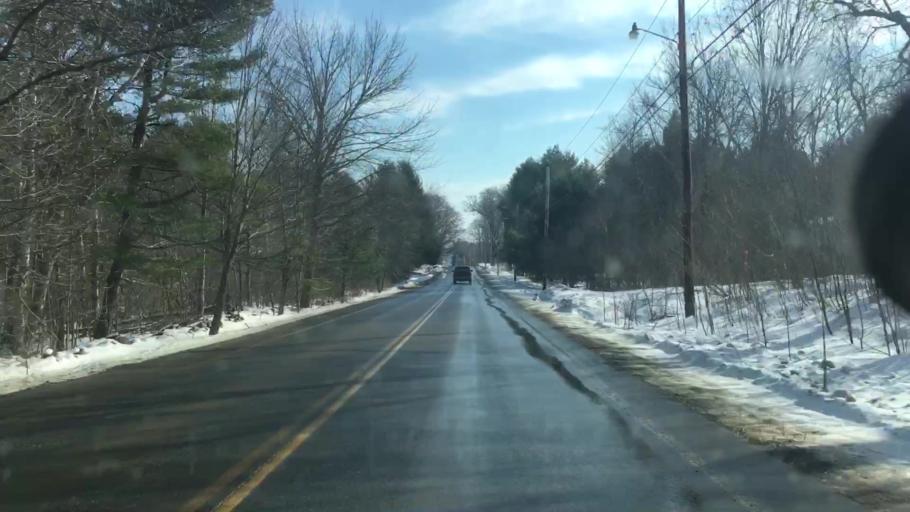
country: US
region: Maine
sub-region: Penobscot County
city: Bangor
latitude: 44.8474
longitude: -68.8386
